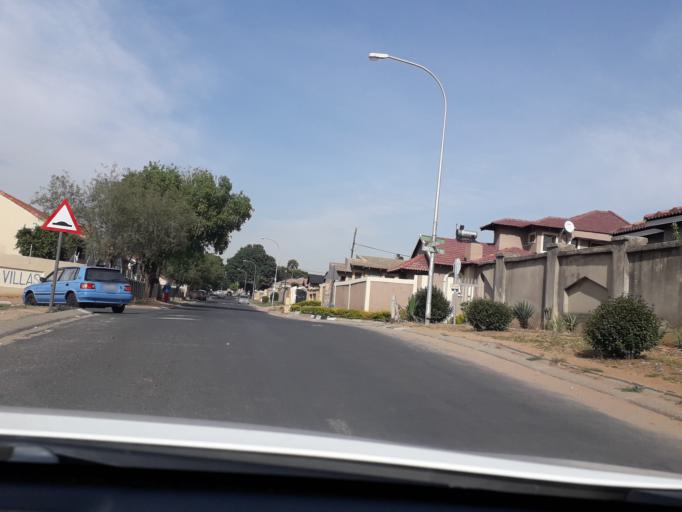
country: ZA
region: Gauteng
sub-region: City of Johannesburg Metropolitan Municipality
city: Modderfontein
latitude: -26.1189
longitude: 28.1045
